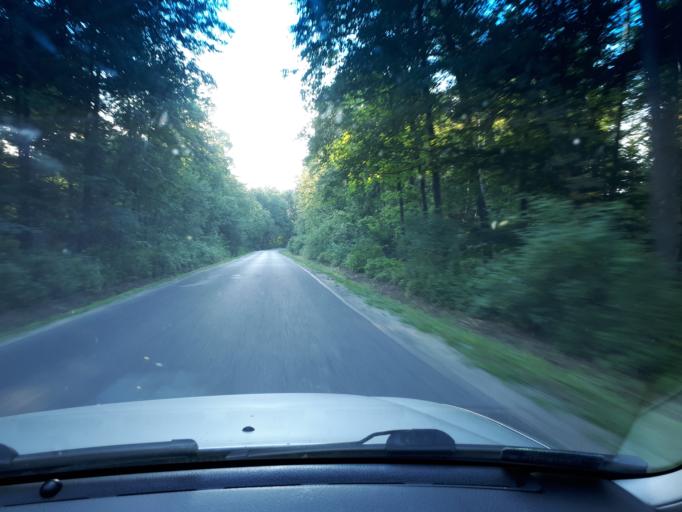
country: PL
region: Subcarpathian Voivodeship
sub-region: Powiat debicki
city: Debica
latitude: 49.9773
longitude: 21.4106
